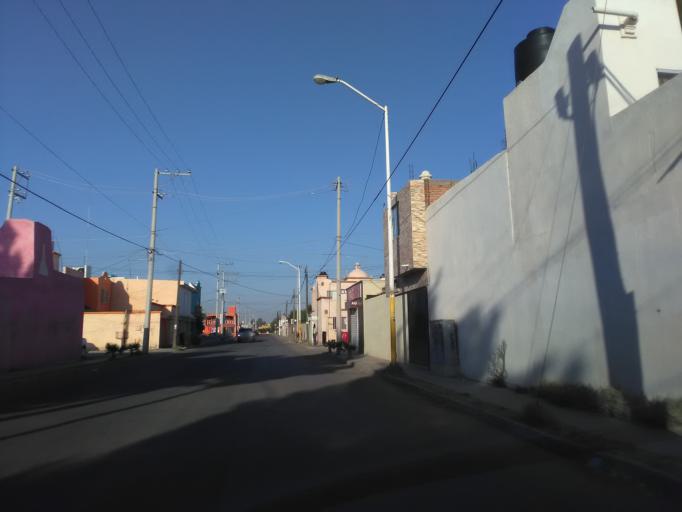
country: MX
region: Durango
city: Victoria de Durango
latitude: 24.0581
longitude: -104.6200
